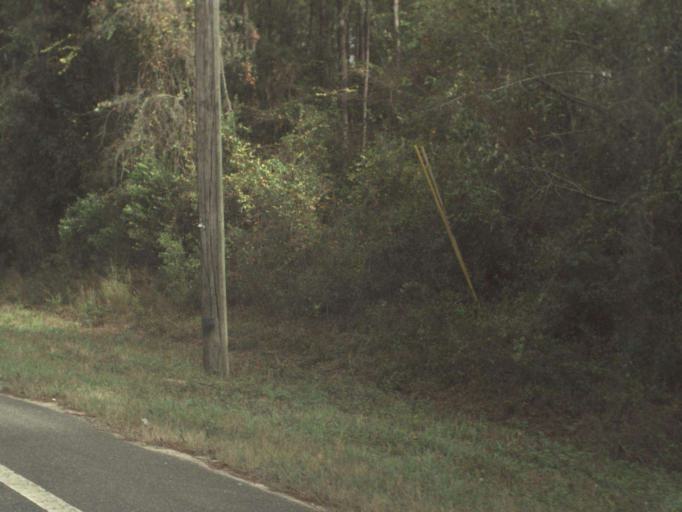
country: US
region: Florida
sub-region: Leon County
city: Woodville
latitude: 30.3606
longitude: -84.2635
